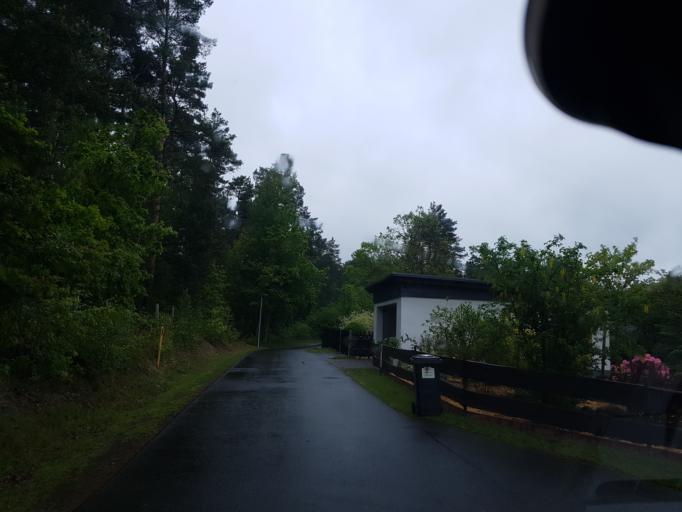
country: DE
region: Brandenburg
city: Tschernitz
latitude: 51.6269
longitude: 14.5956
